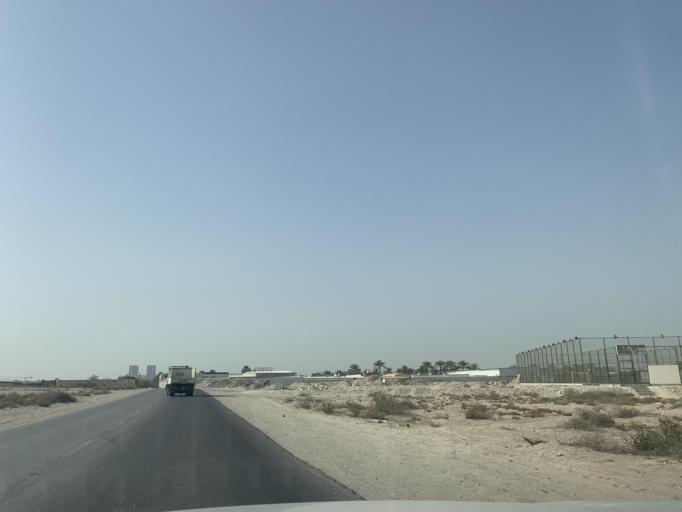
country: BH
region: Central Governorate
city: Madinat Hamad
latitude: 26.1602
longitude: 50.4884
